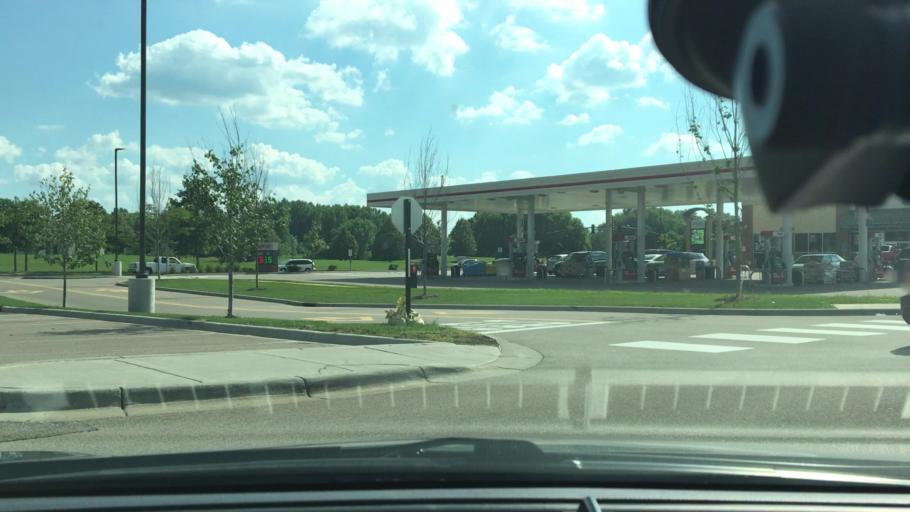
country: US
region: Minnesota
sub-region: Hennepin County
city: New Hope
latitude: 45.0336
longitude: -93.3840
